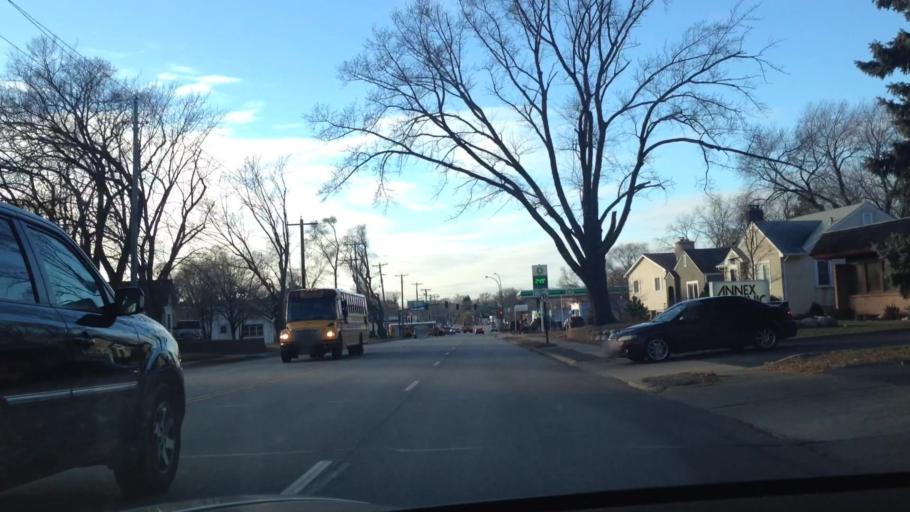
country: US
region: Minnesota
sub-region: Hennepin County
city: Crystal
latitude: 45.0319
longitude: -93.3538
